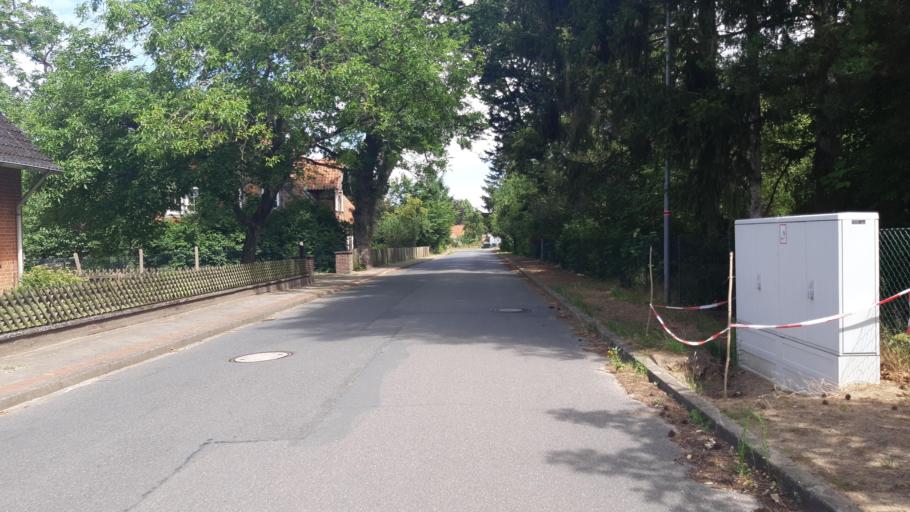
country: DE
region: Lower Saxony
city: Tosterglope
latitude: 53.2392
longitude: 10.7816
